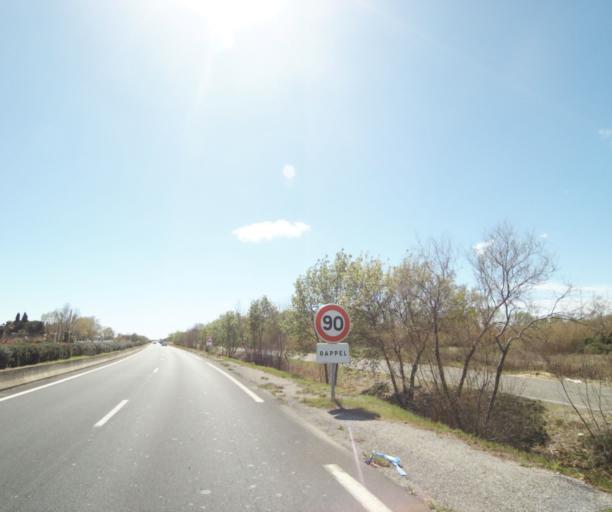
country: FR
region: Languedoc-Roussillon
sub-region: Departement de l'Herault
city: Lattes
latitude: 43.5509
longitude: 3.8934
